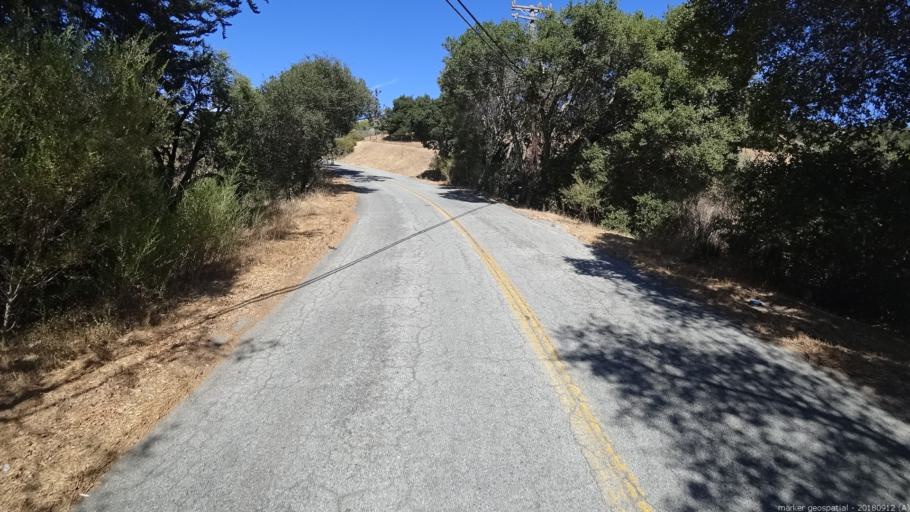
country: US
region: California
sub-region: Monterey County
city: Carmel Valley Village
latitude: 36.4950
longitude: -121.7463
